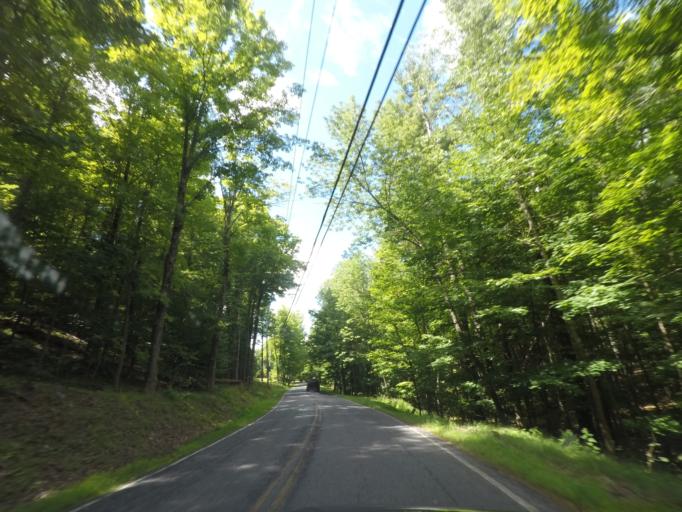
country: US
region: New York
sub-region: Rensselaer County
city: East Greenbush
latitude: 42.6235
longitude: -73.6687
